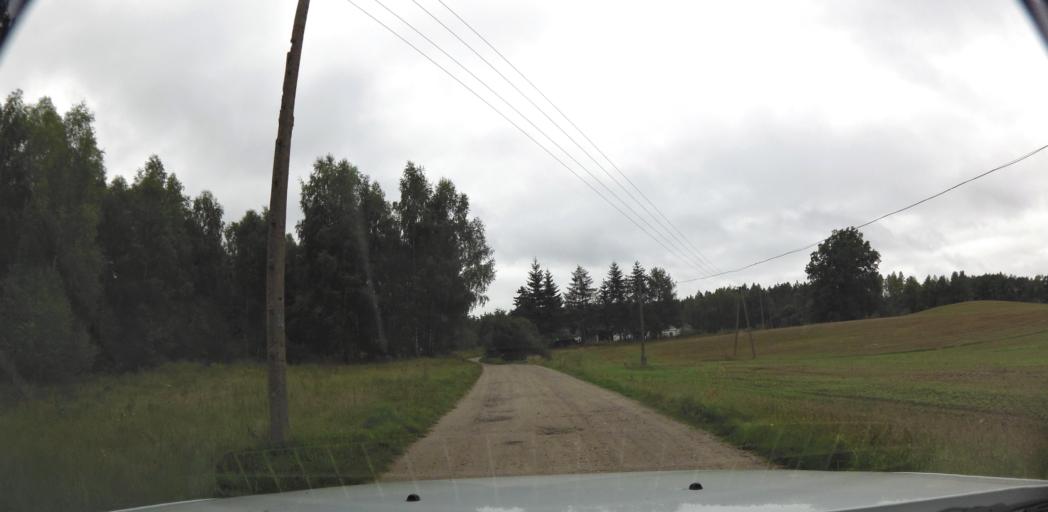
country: PL
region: West Pomeranian Voivodeship
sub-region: Powiat lobeski
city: Wegorzyno
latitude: 53.5236
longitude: 15.5932
